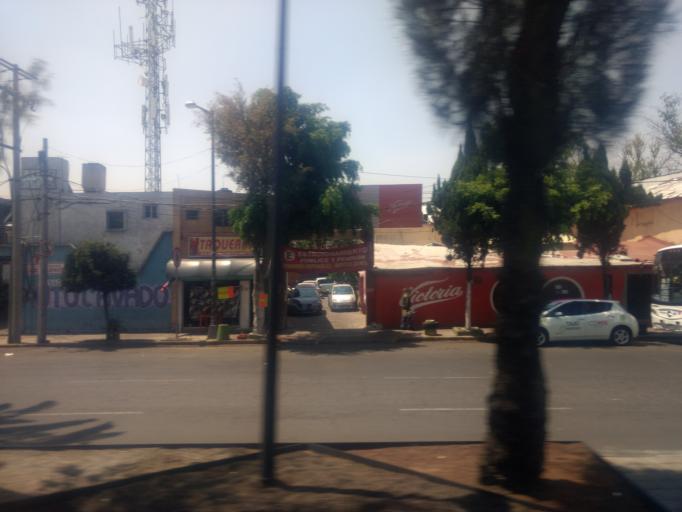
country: MX
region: Mexico
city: Colonia Lindavista
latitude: 19.4804
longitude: -99.1356
